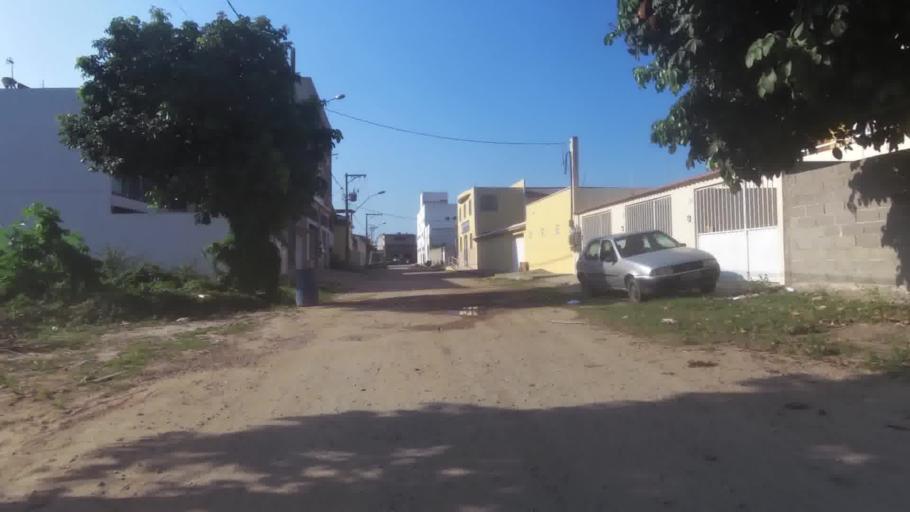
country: BR
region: Espirito Santo
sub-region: Itapemirim
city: Itapemirim
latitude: -21.0121
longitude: -40.8149
